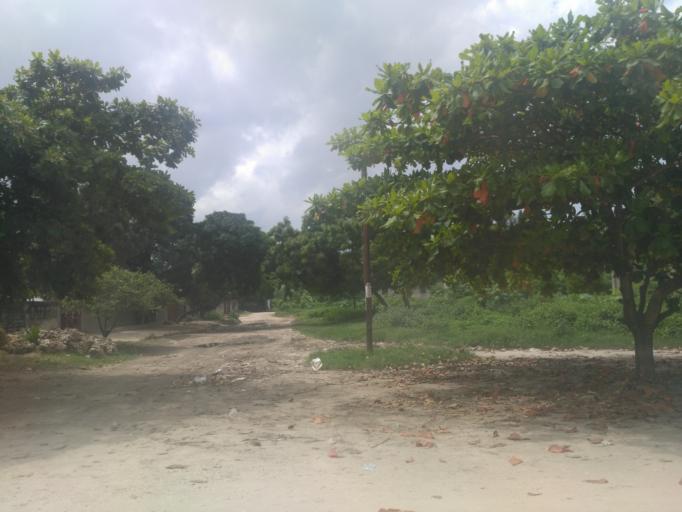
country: TZ
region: Zanzibar Urban/West
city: Zanzibar
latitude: -6.1830
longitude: 39.2225
